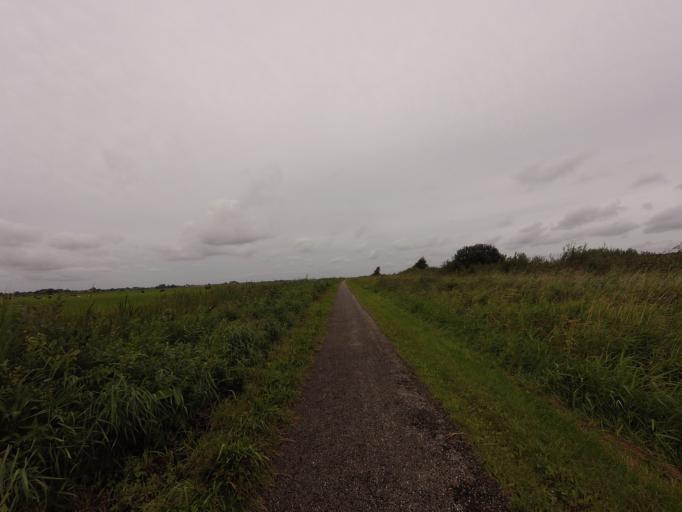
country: NL
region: Overijssel
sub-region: Gemeente Steenwijkerland
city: Blokzijl
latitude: 52.7680
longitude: 5.9211
